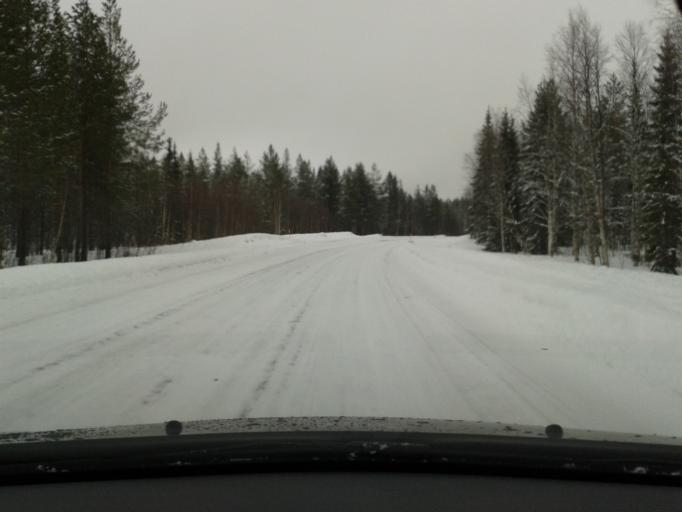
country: SE
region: Vaesterbotten
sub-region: Vilhelmina Kommun
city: Sjoberg
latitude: 64.8664
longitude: 15.8958
